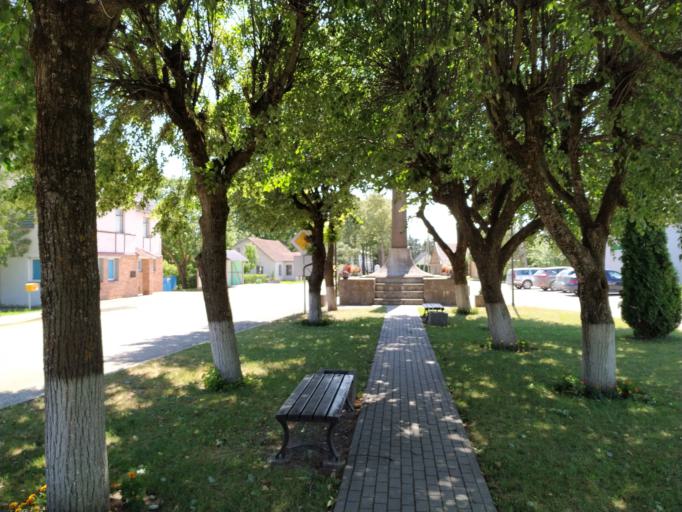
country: LT
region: Panevezys
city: Pasvalys
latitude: 56.2282
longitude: 24.4043
